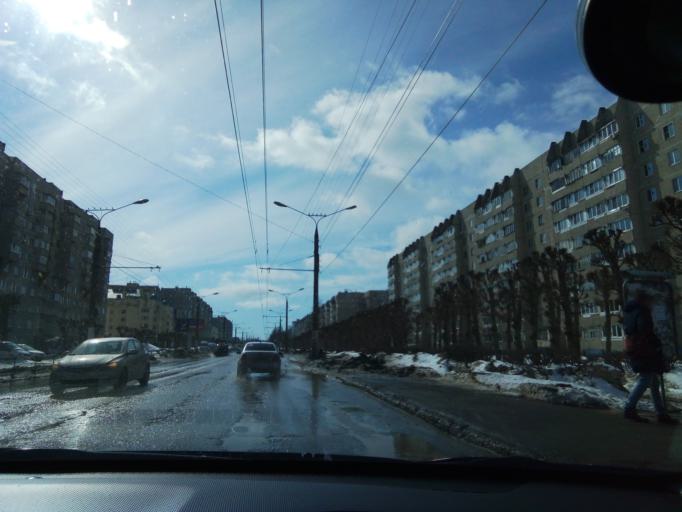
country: RU
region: Chuvashia
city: Novyye Lapsary
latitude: 56.1164
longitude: 47.1912
